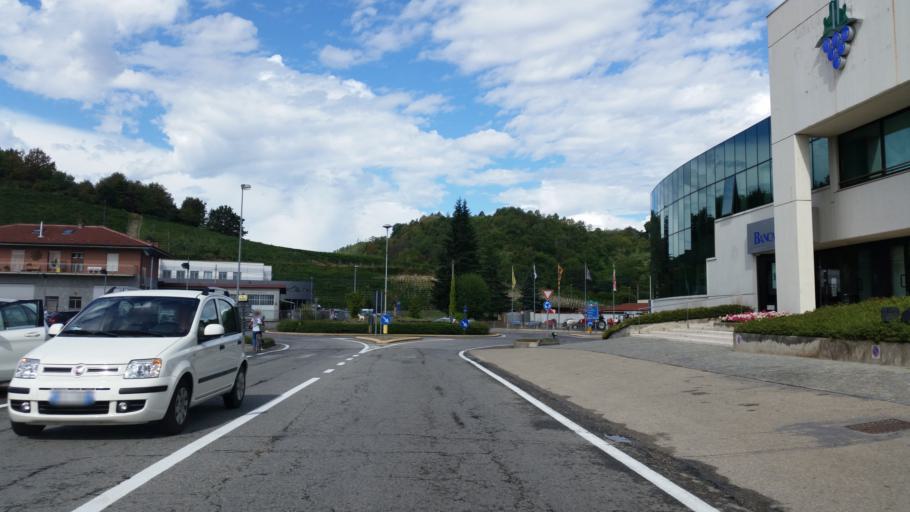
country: IT
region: Piedmont
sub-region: Provincia di Cuneo
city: Vezza d'Alba
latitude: 44.7610
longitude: 8.0104
